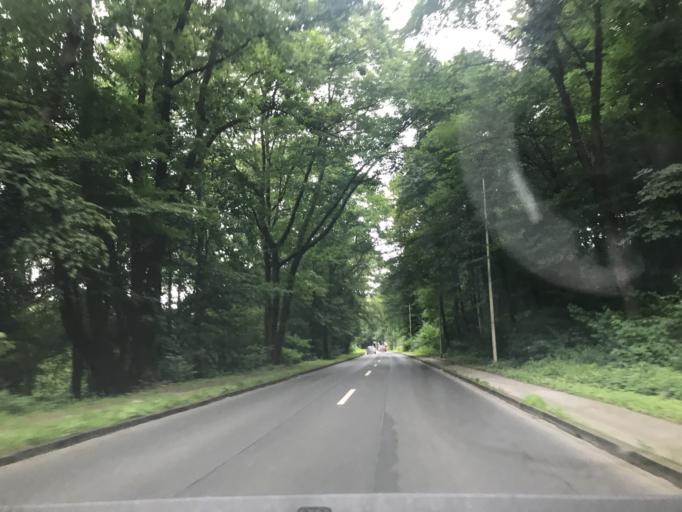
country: DE
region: North Rhine-Westphalia
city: Haan
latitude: 51.1868
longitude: 7.0247
